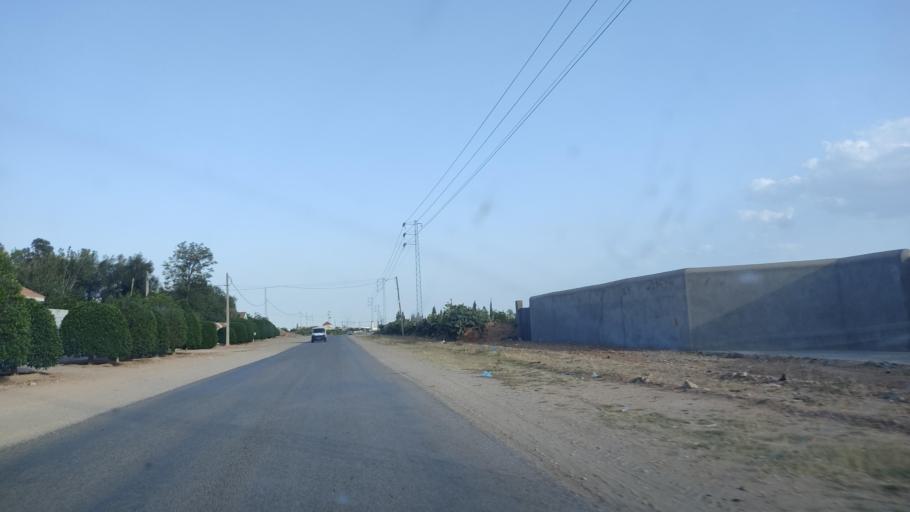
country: TN
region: Safaqis
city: Sfax
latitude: 34.8083
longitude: 10.6656
